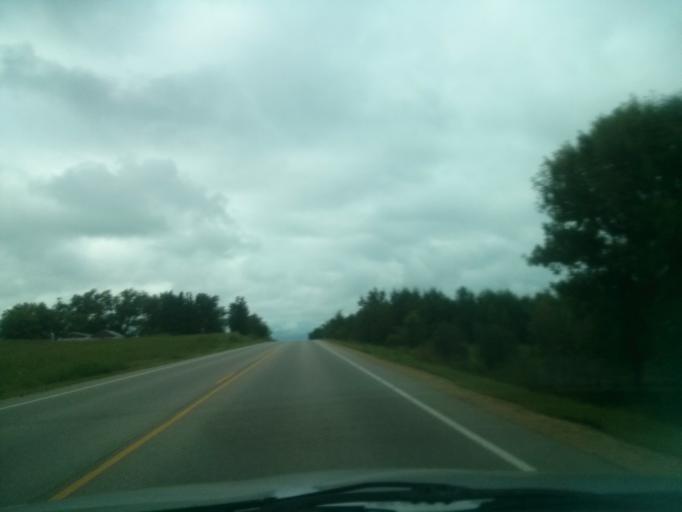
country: US
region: Wisconsin
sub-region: Saint Croix County
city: Baldwin
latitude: 44.8989
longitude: -92.3746
